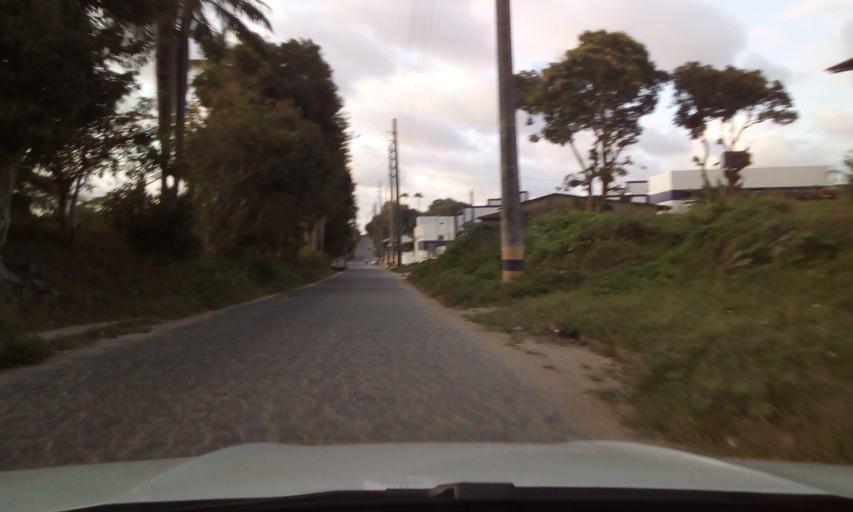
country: BR
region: Paraiba
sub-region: Bayeux
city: Bayeux
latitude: -7.1851
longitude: -34.8919
